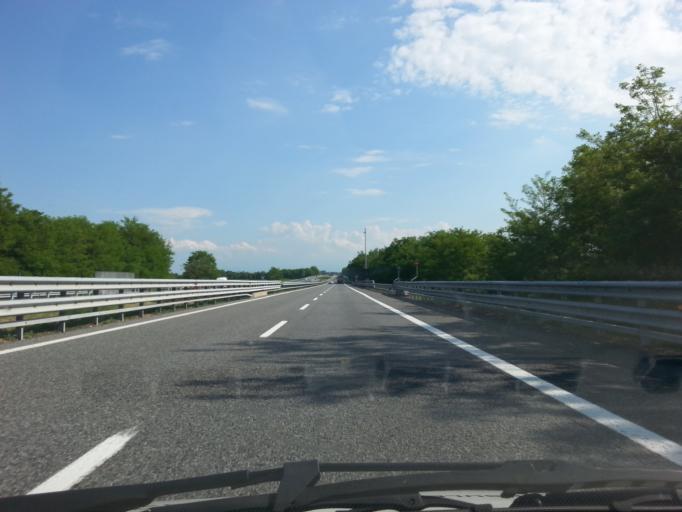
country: IT
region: Piedmont
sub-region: Provincia di Cuneo
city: Caramagna Piemonte
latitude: 44.8060
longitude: 7.7517
